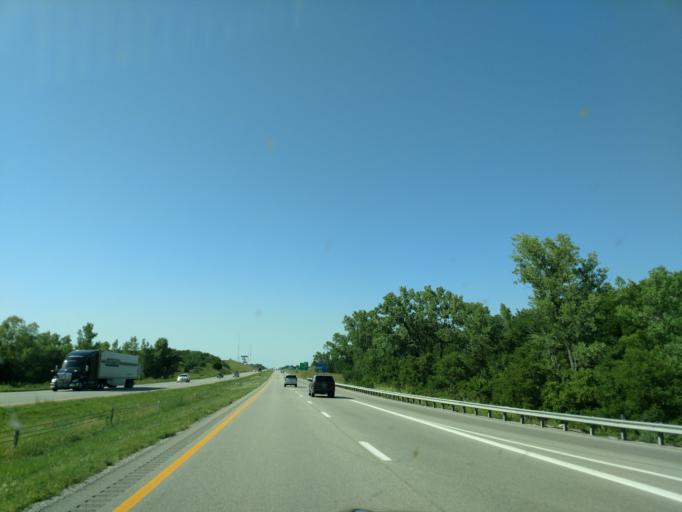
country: US
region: Missouri
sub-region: Buchanan County
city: Saint Joseph
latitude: 39.7111
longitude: -94.7884
